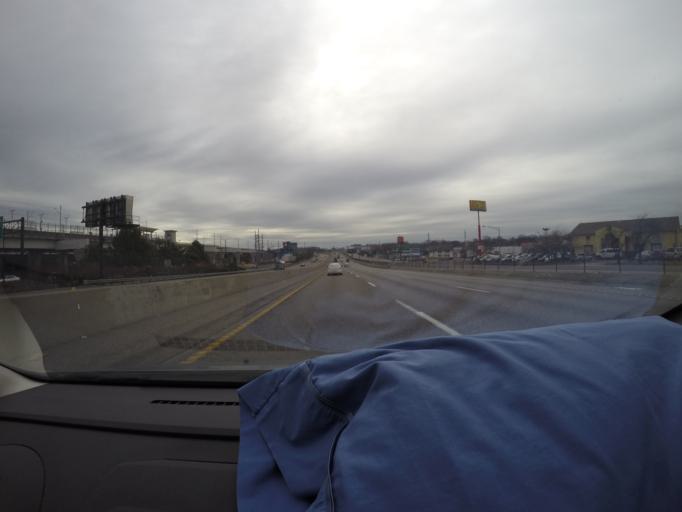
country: US
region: Missouri
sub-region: Saint Louis County
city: Woodson Terrace
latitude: 38.7364
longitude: -90.3576
